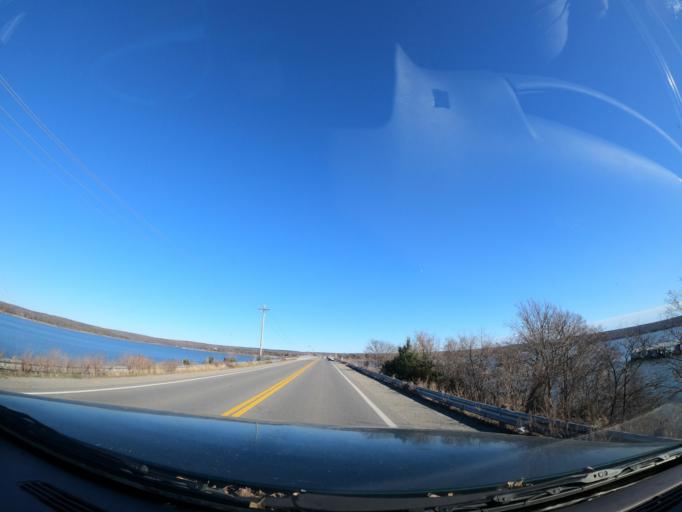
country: US
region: Oklahoma
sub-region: Pittsburg County
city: Longtown
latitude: 35.2392
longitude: -95.5080
